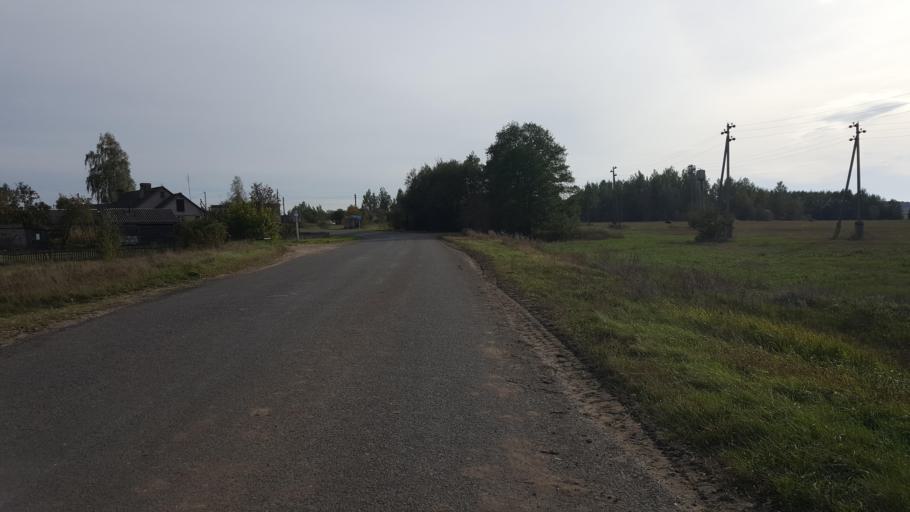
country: BY
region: Brest
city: Kamyanyets
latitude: 52.4161
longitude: 23.8878
